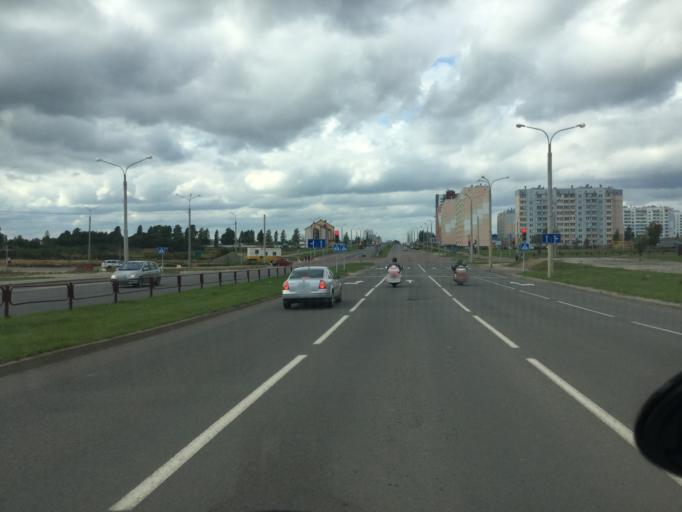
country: BY
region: Vitebsk
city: Vitebsk
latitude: 55.1649
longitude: 30.2672
